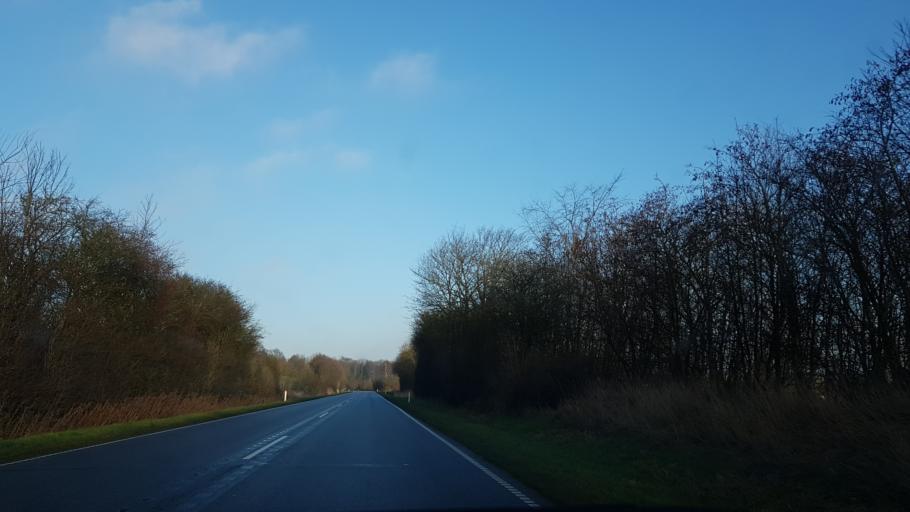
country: DK
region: South Denmark
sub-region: Haderslev Kommune
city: Haderslev
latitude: 55.1853
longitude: 9.4066
